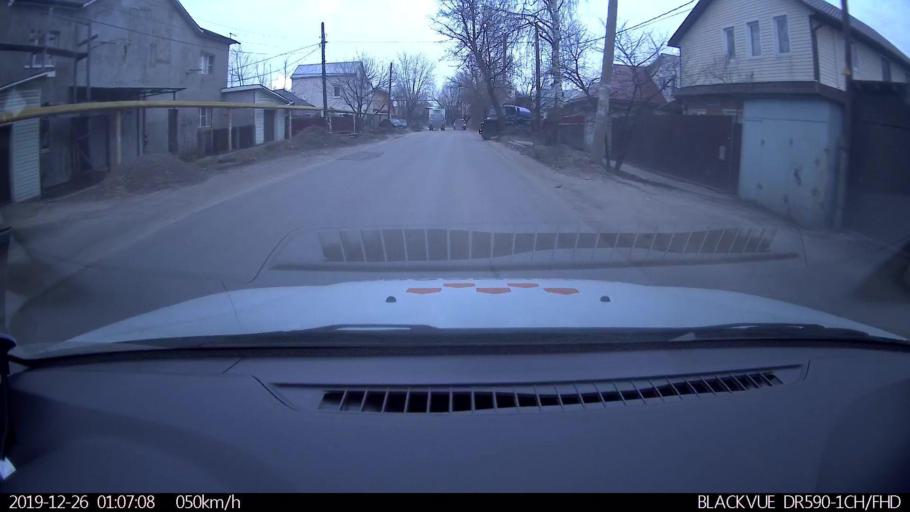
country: RU
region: Nizjnij Novgorod
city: Nizhniy Novgorod
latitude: 56.2800
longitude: 43.9072
